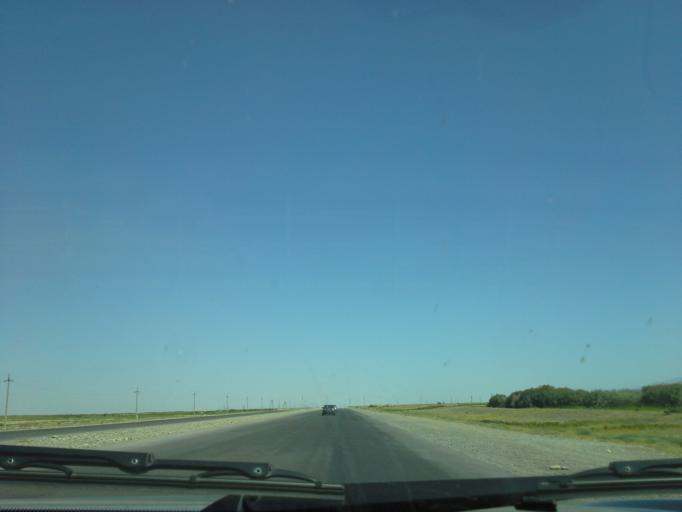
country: TM
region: Balkan
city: Serdar
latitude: 38.9588
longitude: 56.3700
